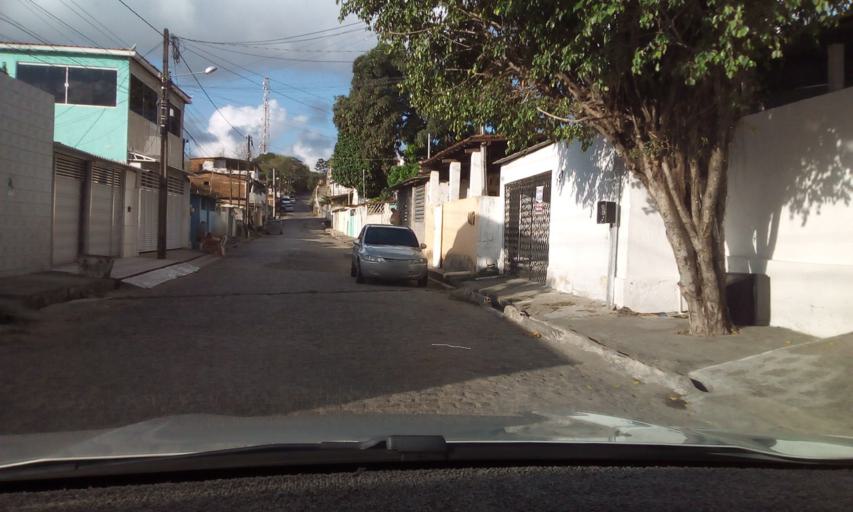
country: BR
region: Paraiba
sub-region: Bayeux
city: Bayeux
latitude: -7.1534
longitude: -34.8958
